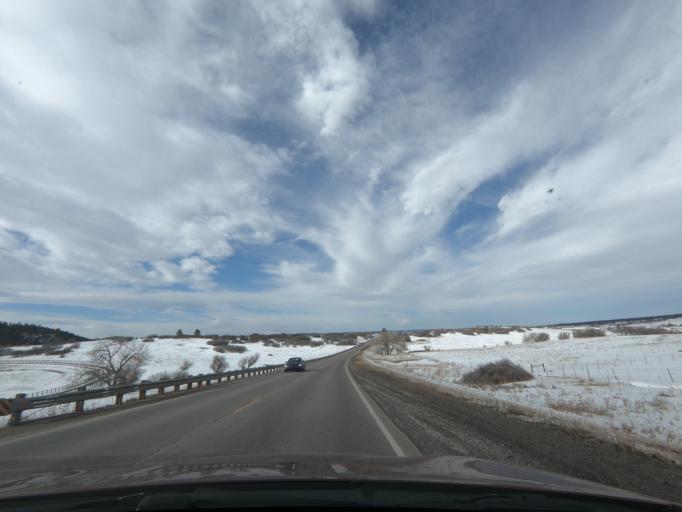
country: US
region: Colorado
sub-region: Douglas County
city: The Pinery
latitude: 39.3544
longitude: -104.7422
